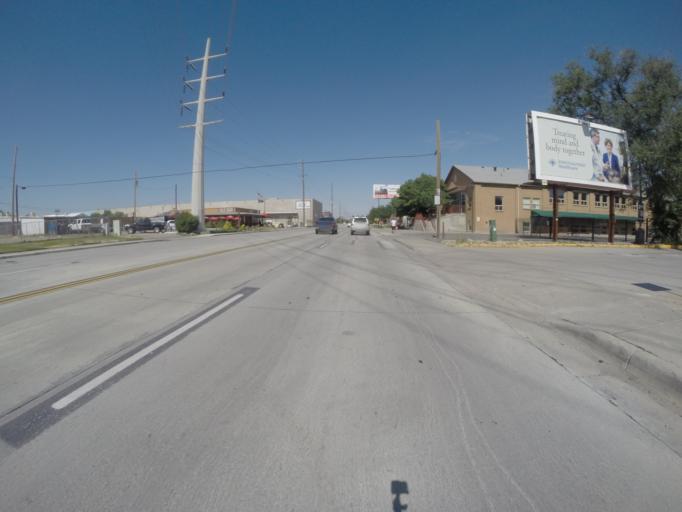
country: US
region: Utah
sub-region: Salt Lake County
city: Salt Lake City
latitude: 40.7417
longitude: -111.8942
